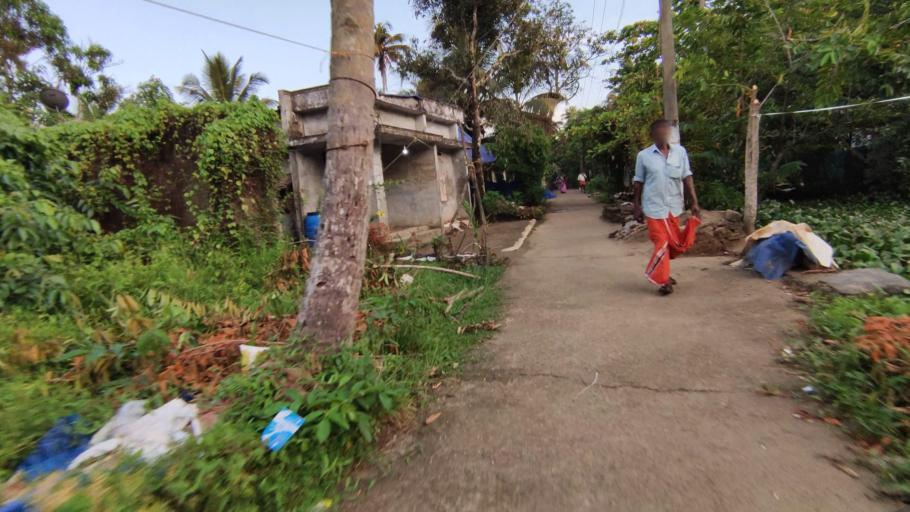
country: IN
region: Kerala
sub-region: Kottayam
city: Kottayam
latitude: 9.5701
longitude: 76.4355
